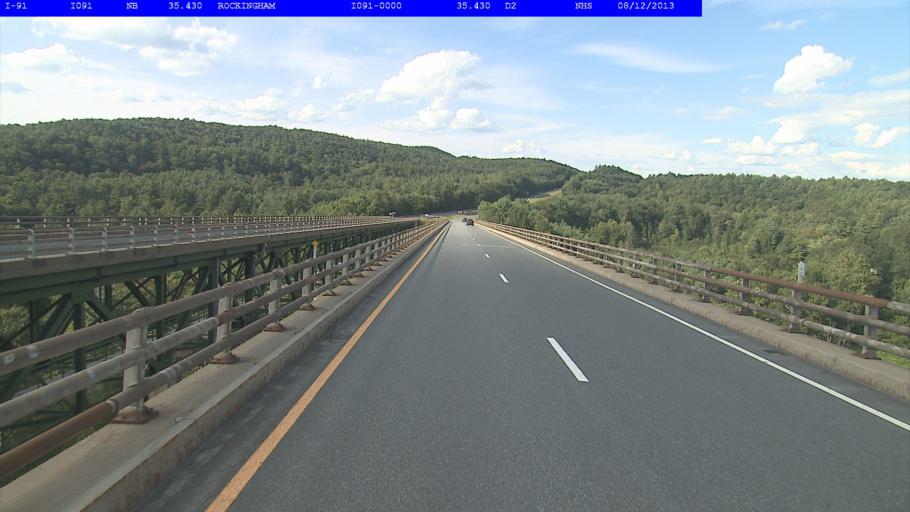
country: US
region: Vermont
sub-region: Windham County
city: Rockingham
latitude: 43.1820
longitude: -72.4630
